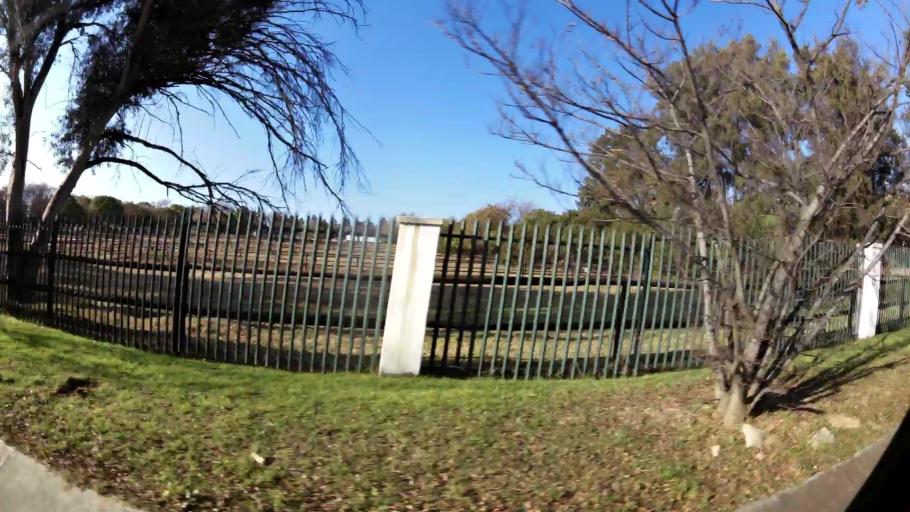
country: ZA
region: Gauteng
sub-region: City of Johannesburg Metropolitan Municipality
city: Diepsloot
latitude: -25.9963
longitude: 28.0391
